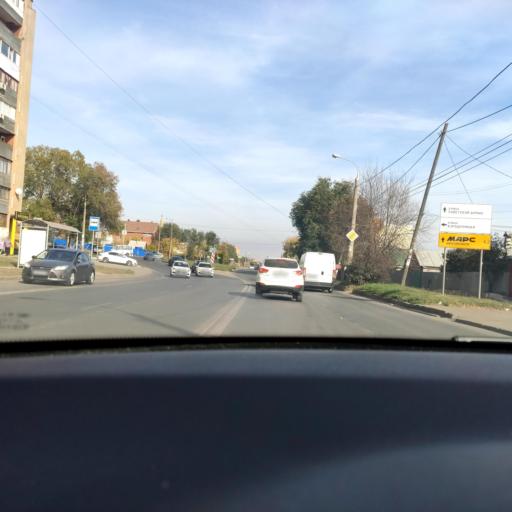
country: RU
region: Samara
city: Samara
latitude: 53.1910
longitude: 50.2118
